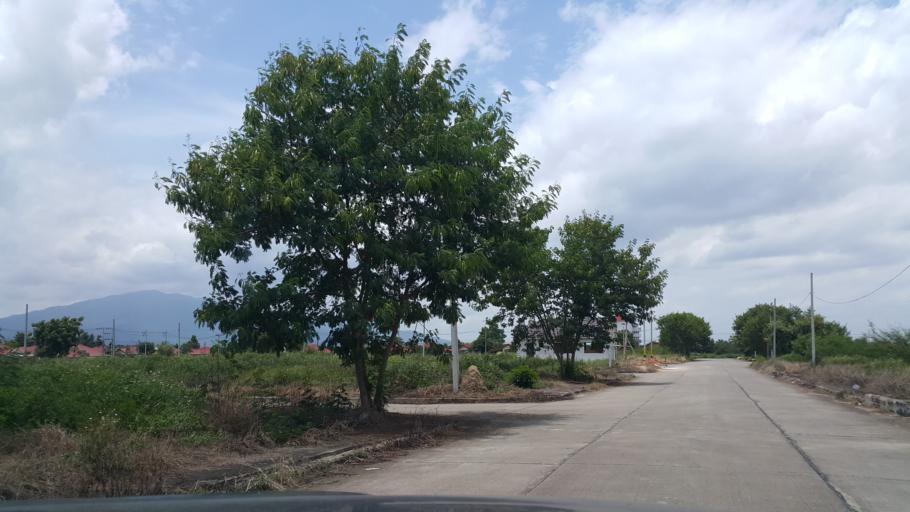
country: TH
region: Chiang Mai
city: Hang Dong
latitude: 18.7068
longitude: 98.9745
